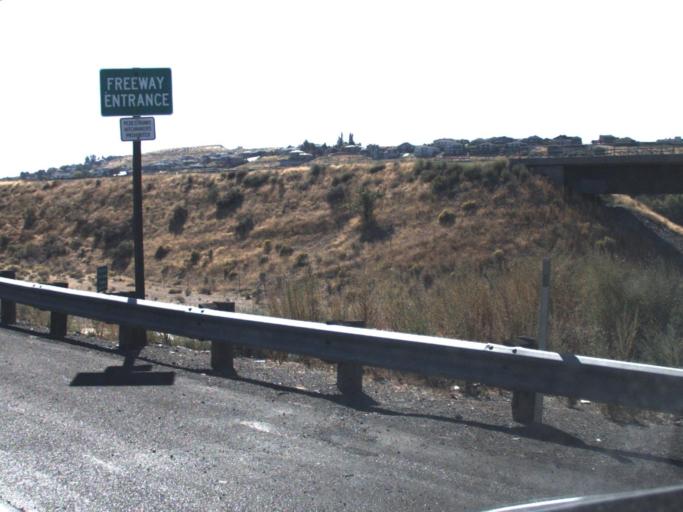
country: US
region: Washington
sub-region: Benton County
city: Richland
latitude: 46.2595
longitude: -119.2877
